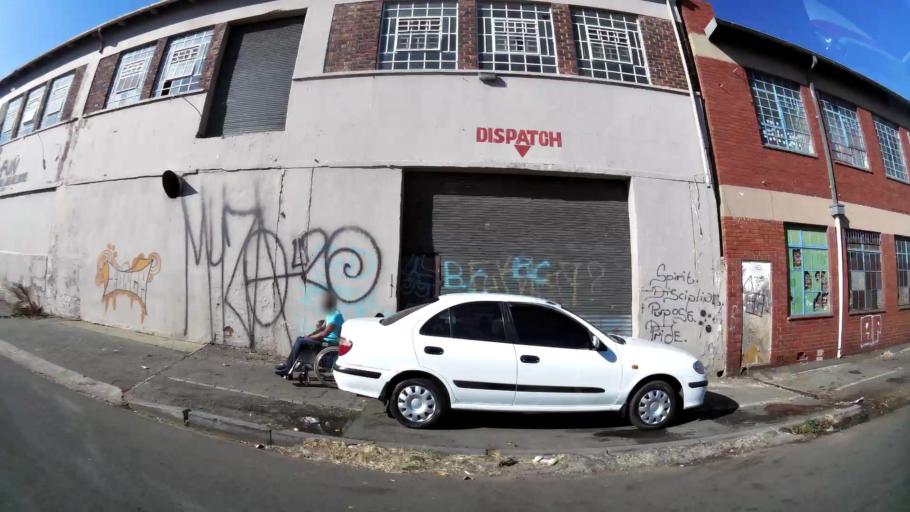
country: ZA
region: Gauteng
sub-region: City of Johannesburg Metropolitan Municipality
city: Johannesburg
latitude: -26.2064
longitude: 28.0603
